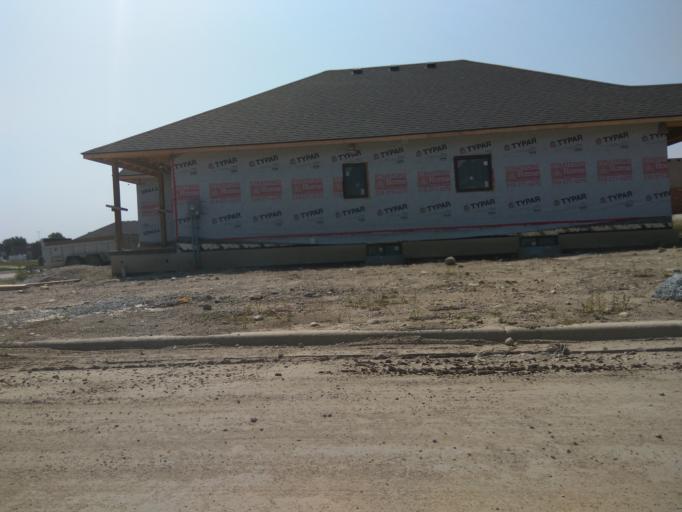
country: CA
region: Ontario
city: Stratford
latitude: 43.3890
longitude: -80.9931
